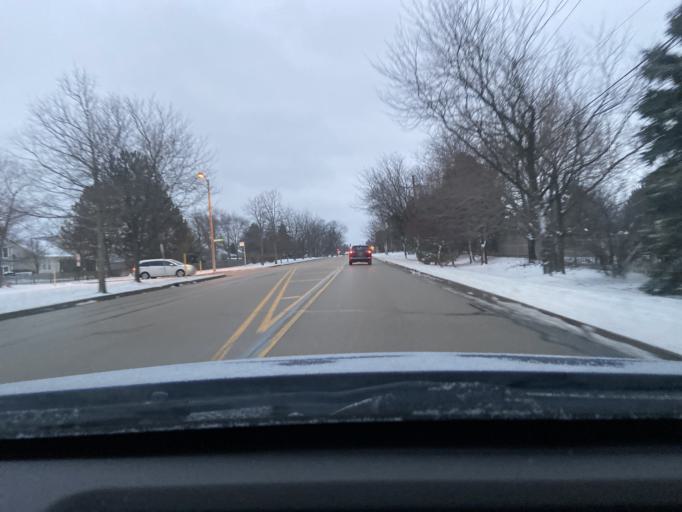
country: US
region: Illinois
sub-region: Lake County
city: Grayslake
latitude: 42.3476
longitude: -88.0241
